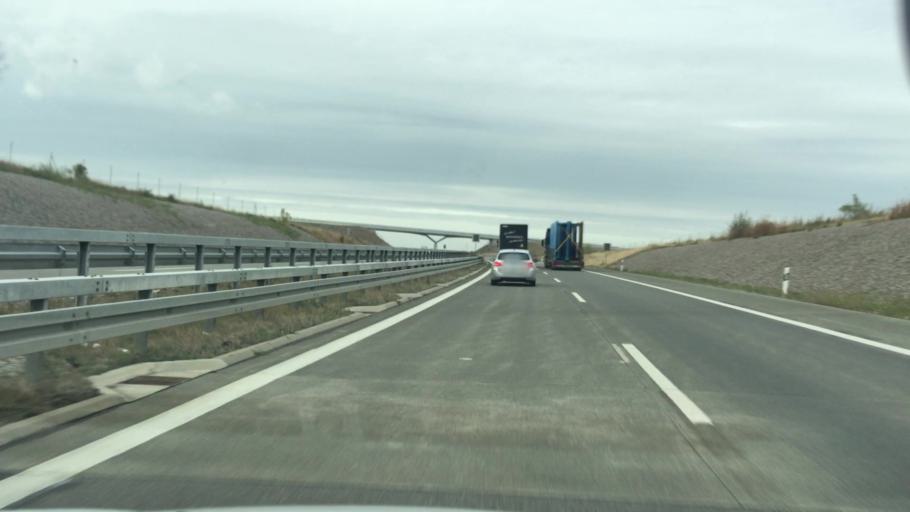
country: DE
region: Saxony
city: Geithain
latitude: 51.0310
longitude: 12.6867
